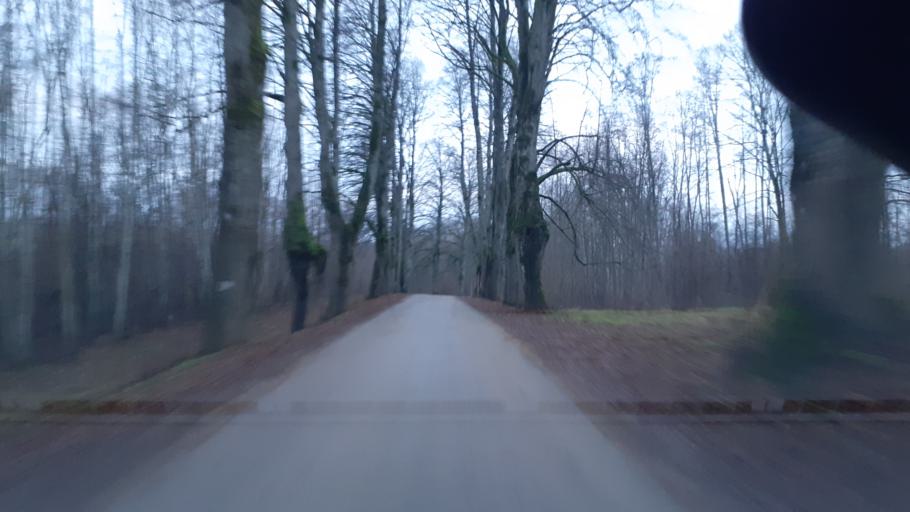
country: LV
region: Alsunga
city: Alsunga
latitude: 56.9006
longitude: 21.7001
